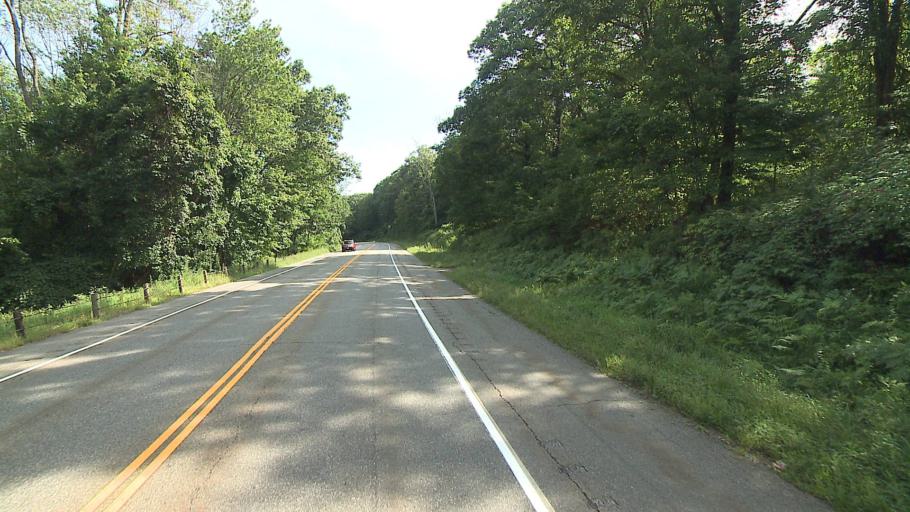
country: US
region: Connecticut
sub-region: Litchfield County
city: Litchfield
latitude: 41.7510
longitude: -73.1599
